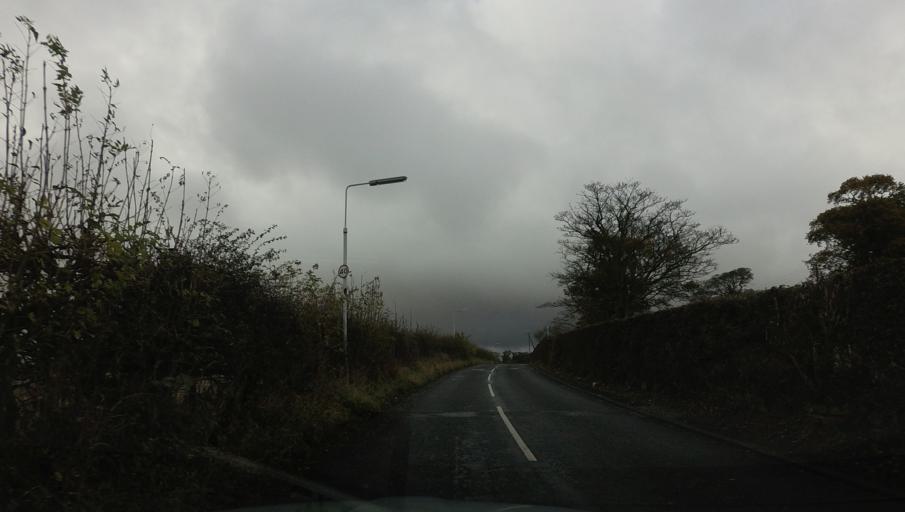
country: GB
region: Scotland
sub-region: Fife
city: East Wemyss
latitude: 56.1432
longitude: -3.0937
